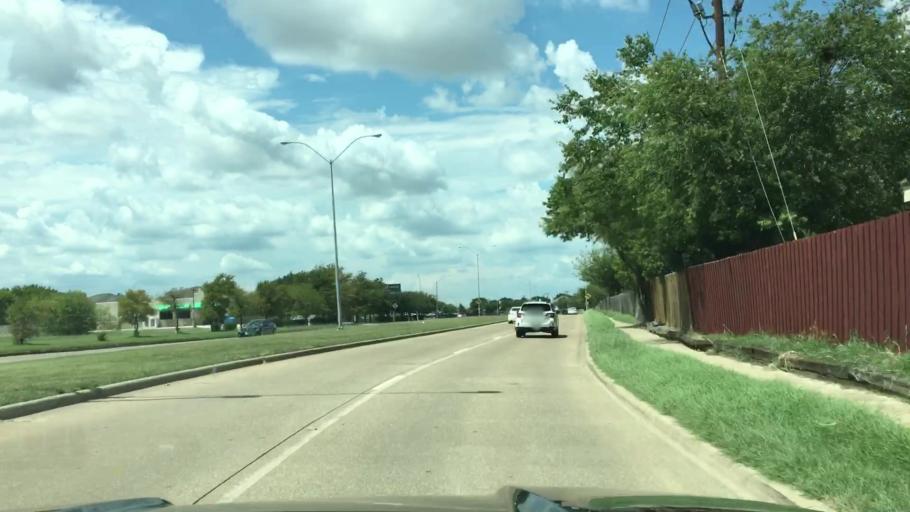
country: US
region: Texas
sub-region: Tarrant County
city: Blue Mound
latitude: 32.8617
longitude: -97.3345
